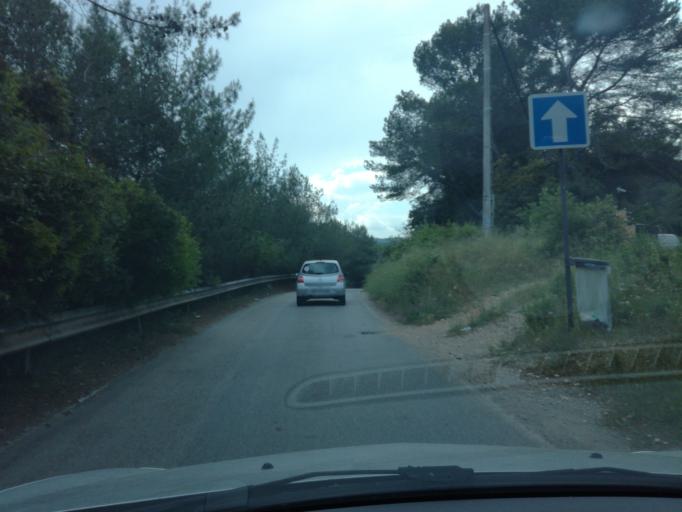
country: FR
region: Provence-Alpes-Cote d'Azur
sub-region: Departement des Alpes-Maritimes
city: Vallauris
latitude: 43.6041
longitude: 7.0716
